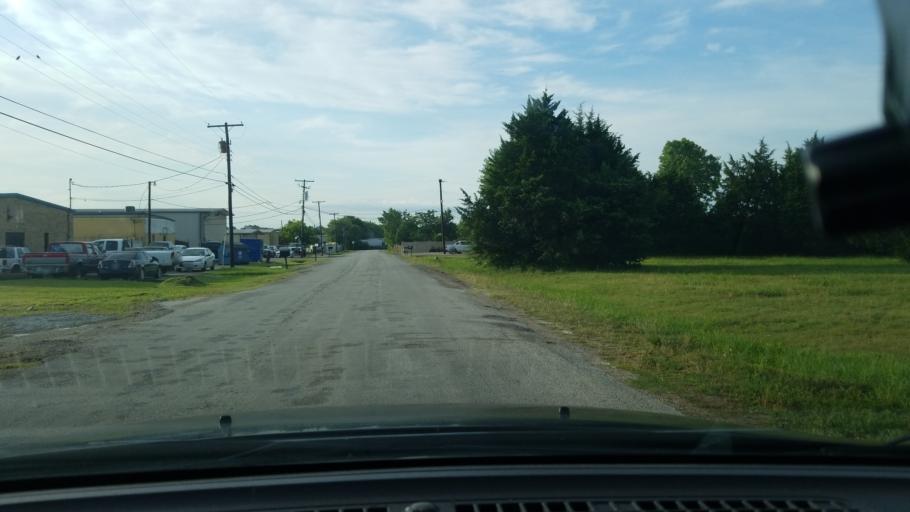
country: US
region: Texas
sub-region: Dallas County
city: Mesquite
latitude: 32.7963
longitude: -96.6213
